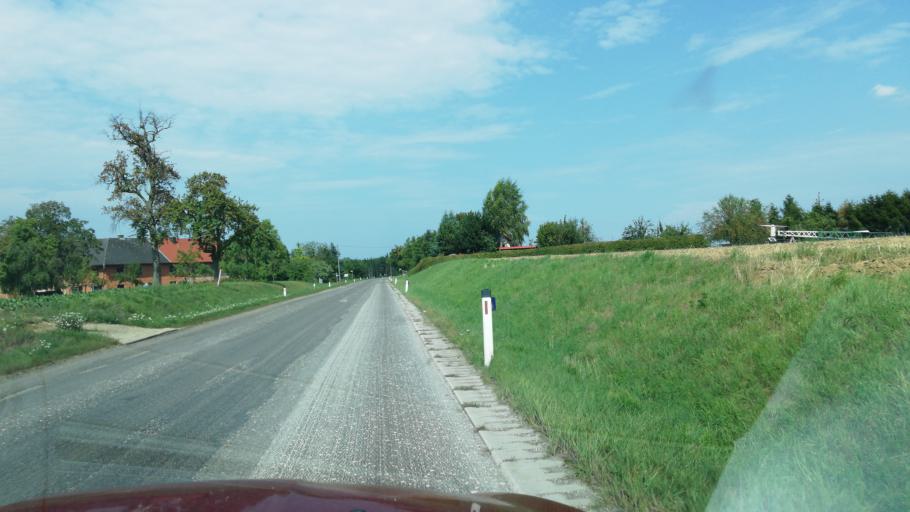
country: AT
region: Upper Austria
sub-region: Politischer Bezirk Steyr-Land
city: Sierning
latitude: 48.1031
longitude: 14.3183
